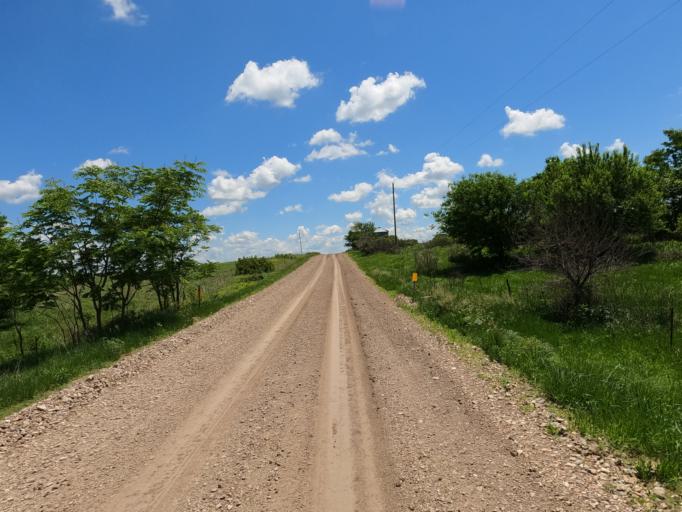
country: US
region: Kansas
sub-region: Marion County
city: Marion
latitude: 38.2165
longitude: -96.7747
